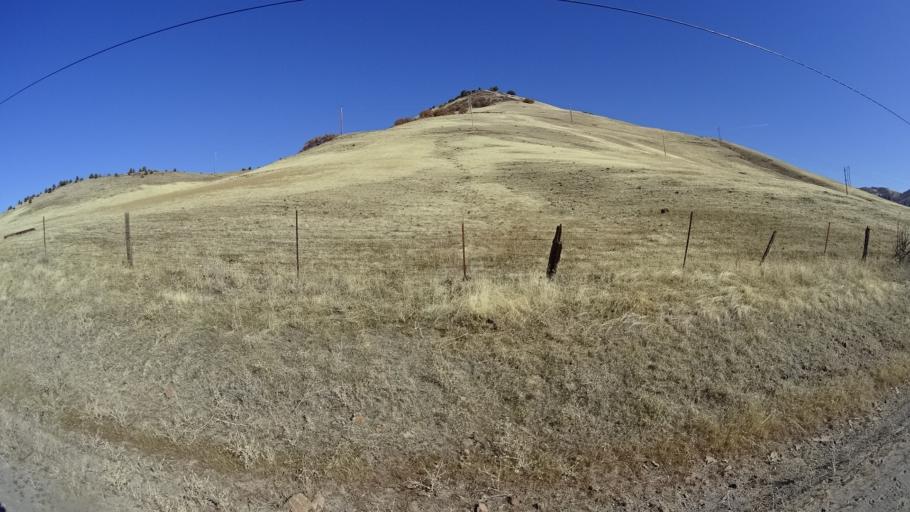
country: US
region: California
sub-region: Siskiyou County
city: Montague
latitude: 41.7957
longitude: -122.3655
